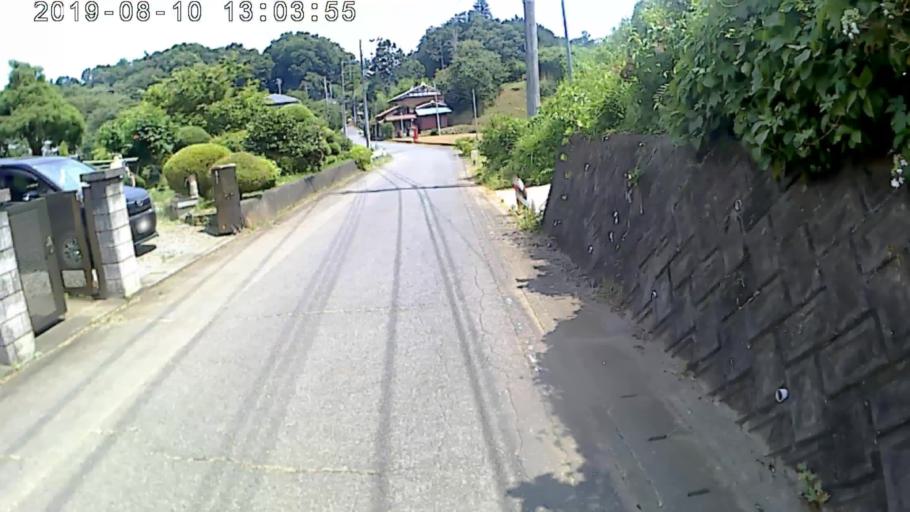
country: JP
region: Yamanashi
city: Uenohara
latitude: 35.6340
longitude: 139.0681
